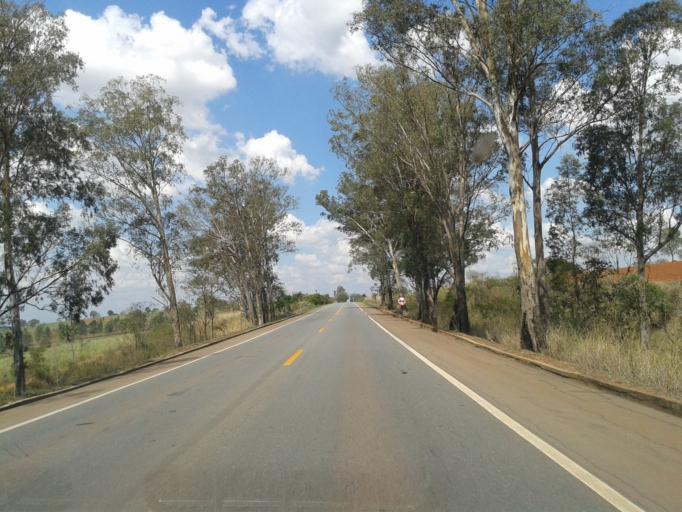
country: BR
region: Minas Gerais
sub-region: Luz
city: Luz
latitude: -19.7784
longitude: -45.7419
